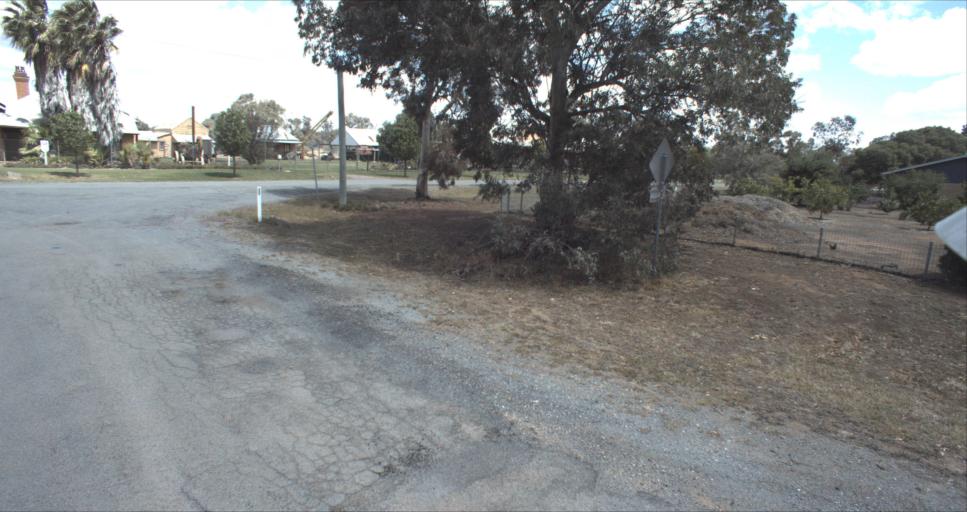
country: AU
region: New South Wales
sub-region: Murrumbidgee Shire
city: Darlington Point
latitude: -34.5194
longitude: 146.1818
